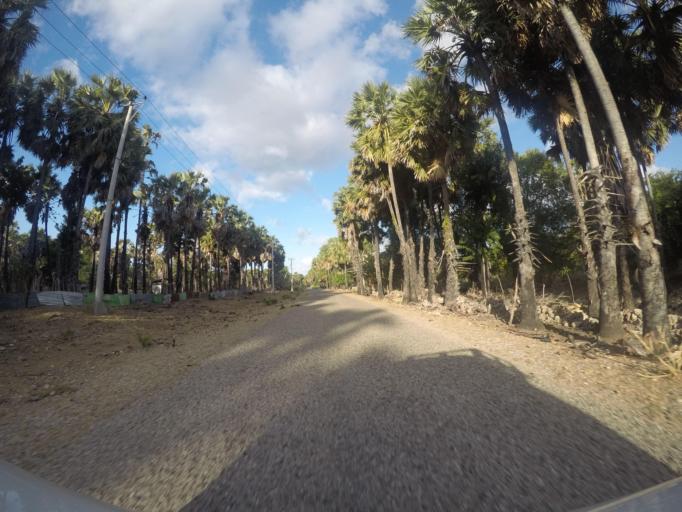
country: TL
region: Lautem
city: Lospalos
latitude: -8.3294
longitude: 126.9630
